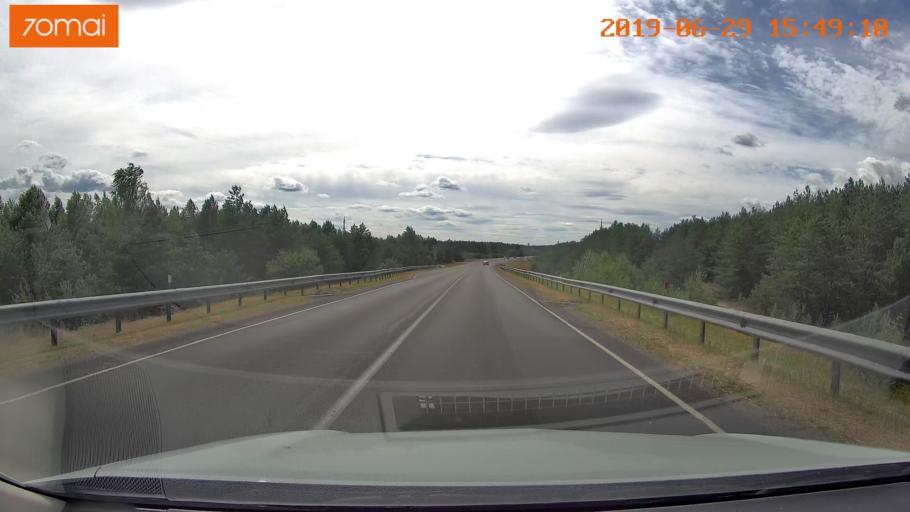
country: BY
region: Brest
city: Davyd-Haradok
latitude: 52.2360
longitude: 27.2482
